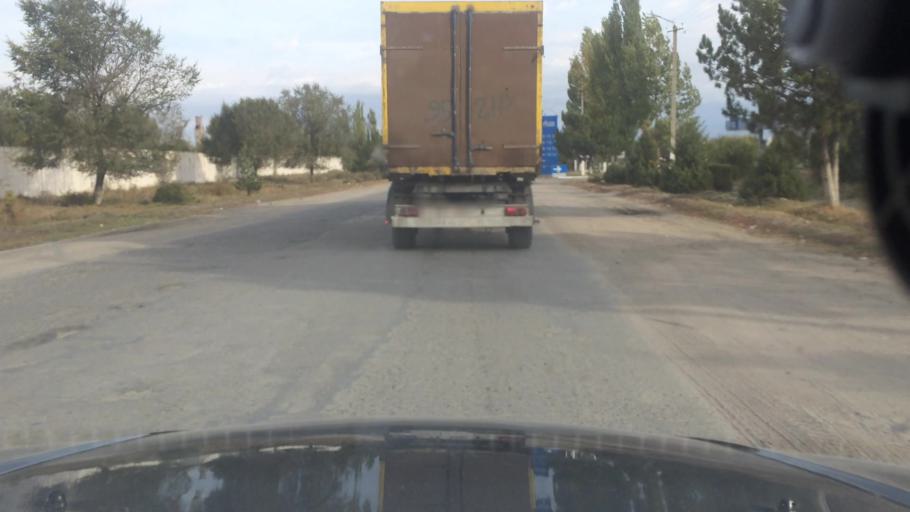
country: KG
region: Ysyk-Koel
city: Karakol
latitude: 42.5154
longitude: 78.3858
